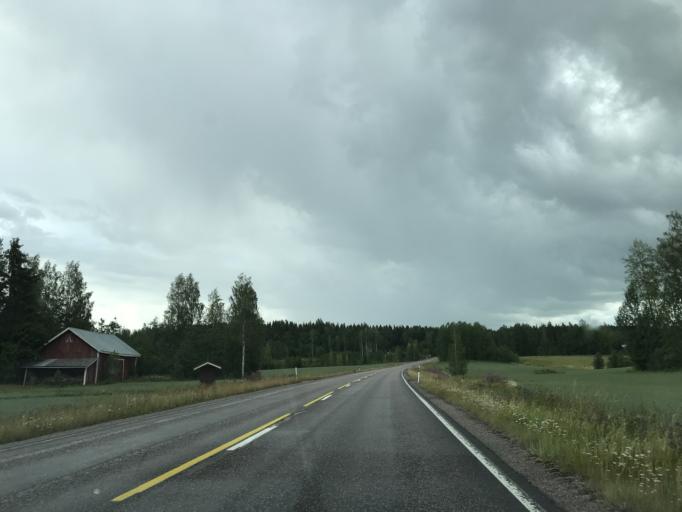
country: FI
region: Paijanne Tavastia
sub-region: Lahti
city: Orimattila
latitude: 60.7905
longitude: 25.6423
